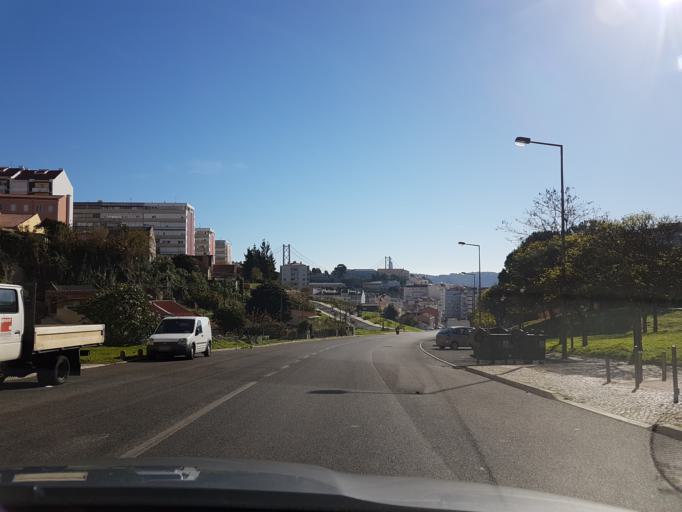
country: PT
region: Lisbon
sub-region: Oeiras
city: Alges
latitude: 38.7074
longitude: -9.1937
